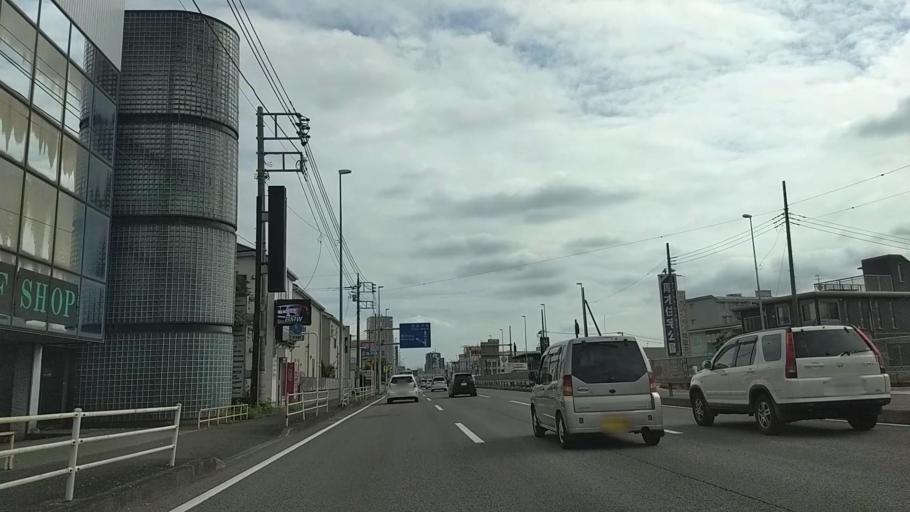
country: JP
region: Kanagawa
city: Atsugi
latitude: 35.4573
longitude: 139.3593
